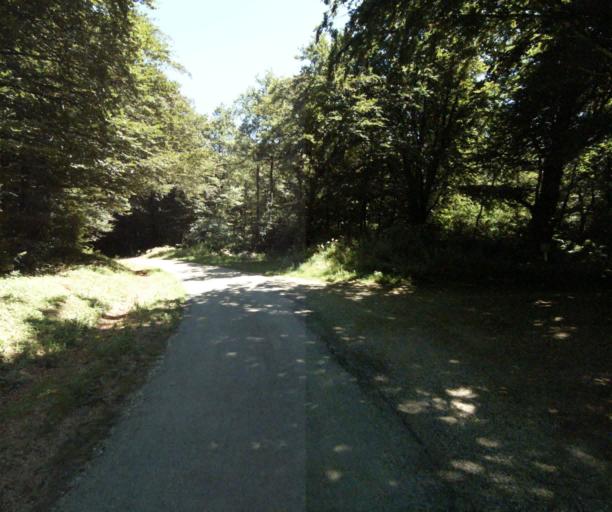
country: FR
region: Midi-Pyrenees
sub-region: Departement du Tarn
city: Dourgne
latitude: 43.4293
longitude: 2.1540
